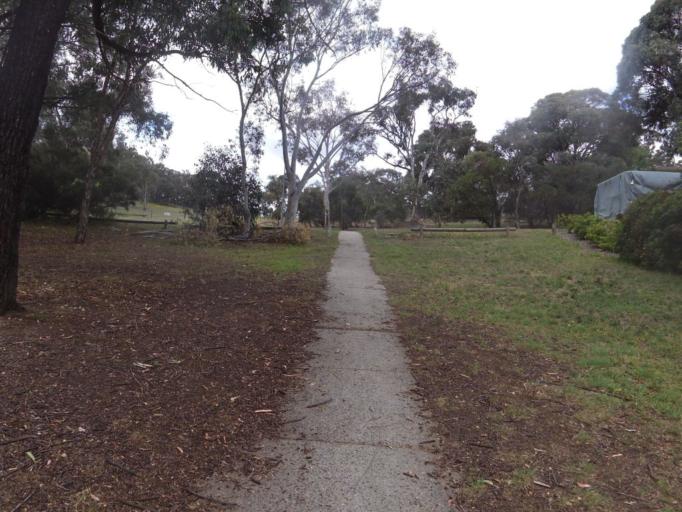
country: AU
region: Australian Capital Territory
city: Macarthur
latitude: -35.4016
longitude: 149.1297
